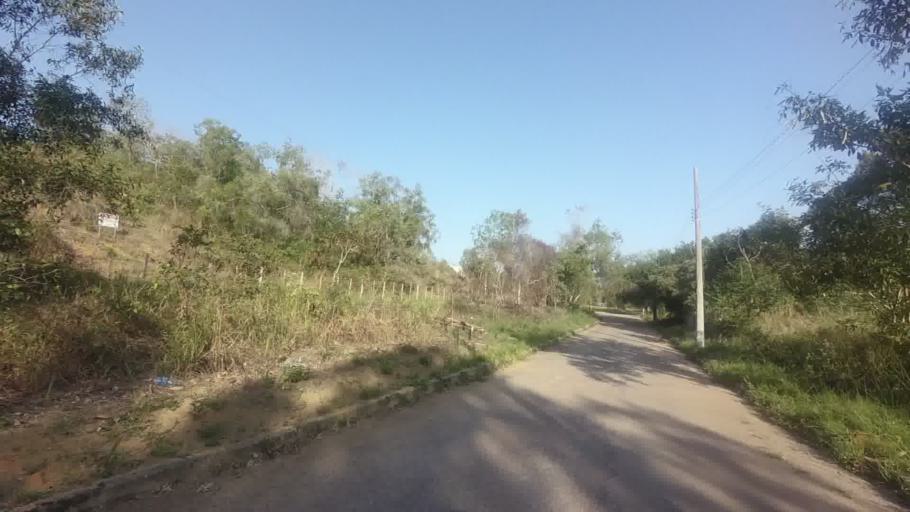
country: BR
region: Espirito Santo
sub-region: Guarapari
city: Guarapari
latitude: -20.7219
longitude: -40.5404
